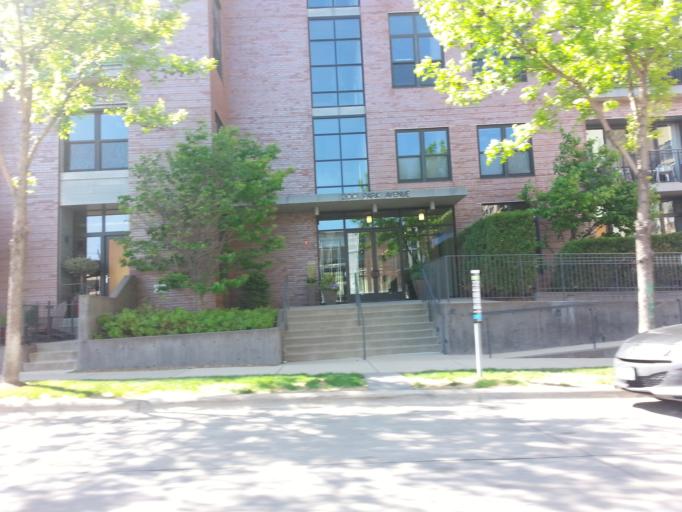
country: US
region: Minnesota
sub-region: Hennepin County
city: Minneapolis
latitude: 44.9784
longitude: -93.2581
